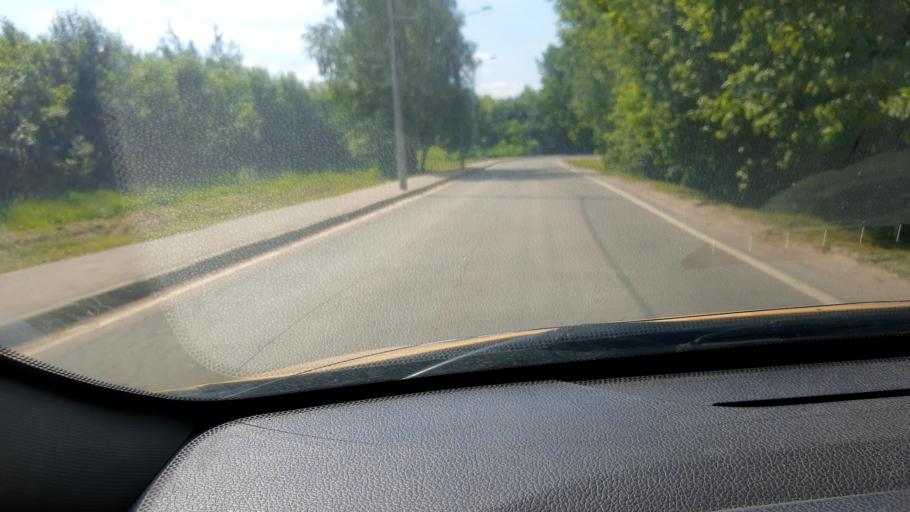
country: RU
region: Moskovskaya
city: Vatutinki
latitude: 55.5023
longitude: 37.3229
